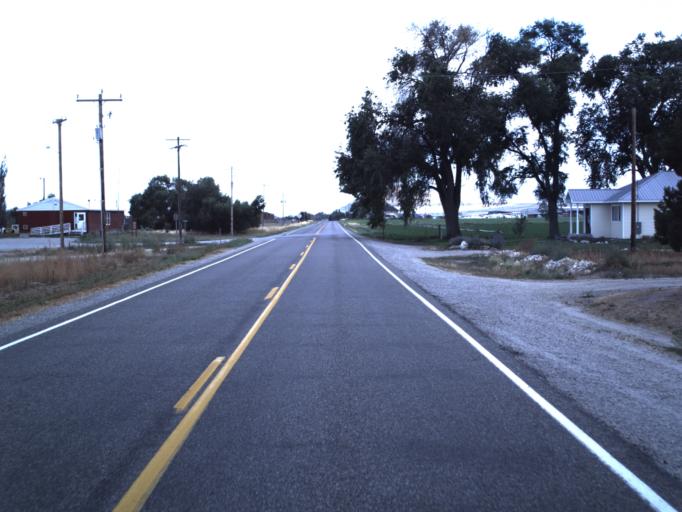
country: US
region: Utah
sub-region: Cache County
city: Lewiston
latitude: 41.9927
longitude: -111.9548
